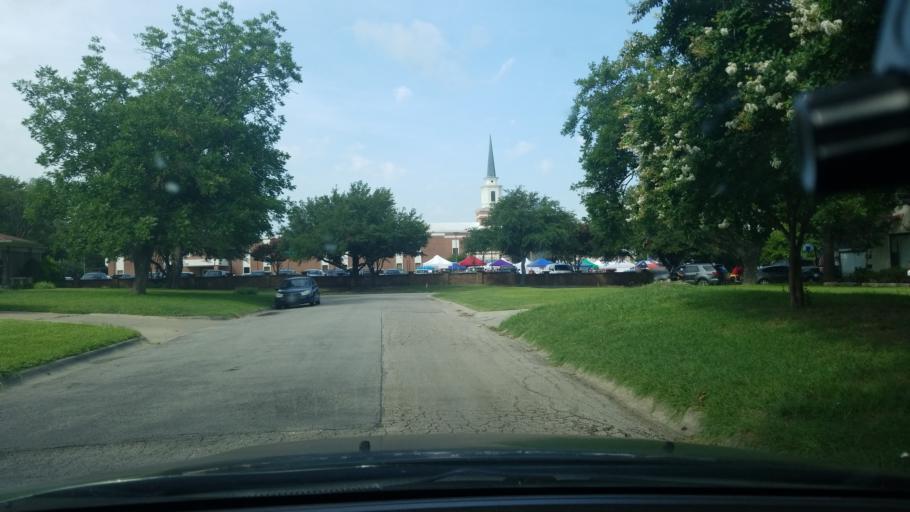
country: US
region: Texas
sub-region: Dallas County
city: Highland Park
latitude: 32.8301
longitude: -96.7056
